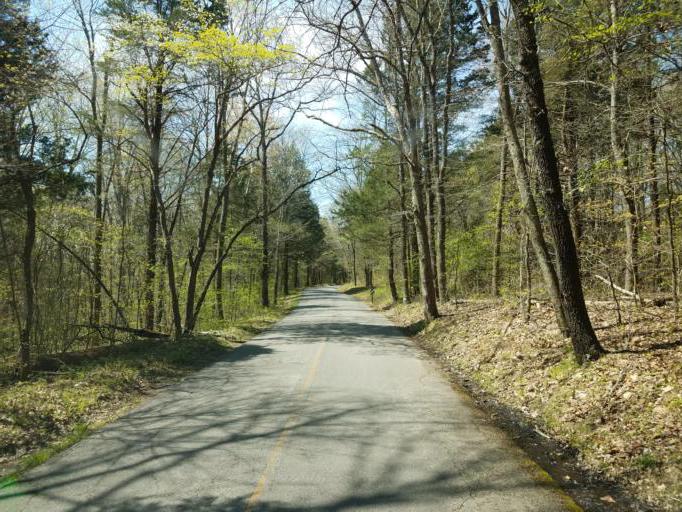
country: US
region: Kentucky
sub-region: Barren County
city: Cave City
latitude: 37.1614
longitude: -86.0428
